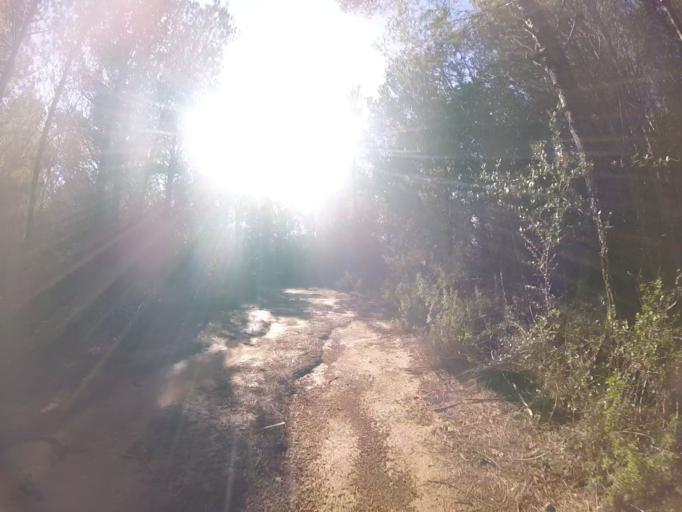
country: ES
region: Valencia
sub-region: Provincia de Castello
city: Sarratella
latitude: 40.2854
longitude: 0.0642
